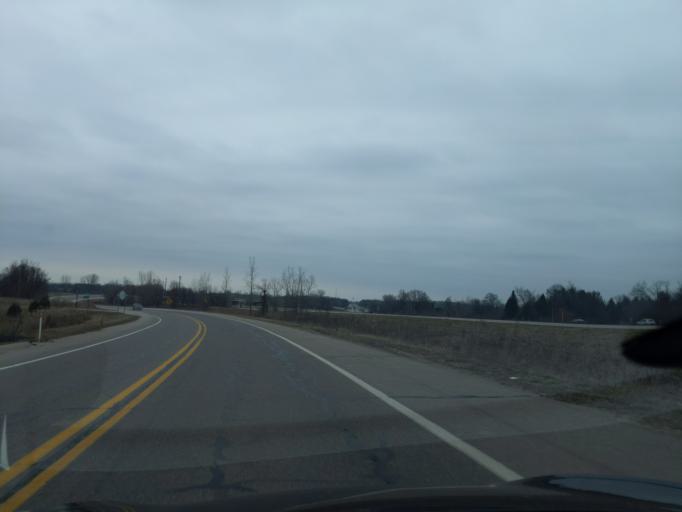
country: US
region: Michigan
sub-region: Eaton County
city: Dimondale
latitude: 42.6536
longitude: -84.6896
